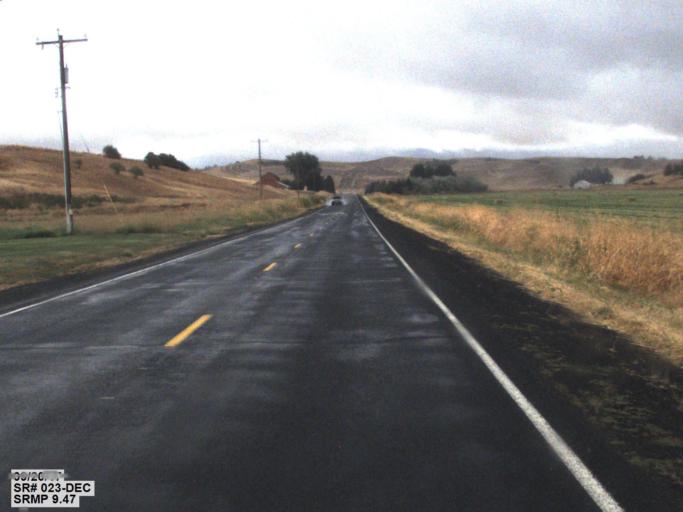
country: US
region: Washington
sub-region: Whitman County
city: Colfax
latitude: 47.0482
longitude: -117.5164
